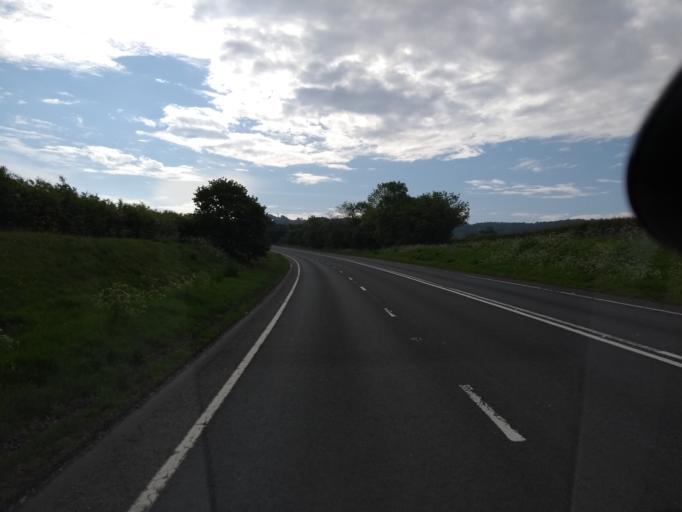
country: GB
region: England
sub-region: Devon
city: Axminster
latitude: 50.7684
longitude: -3.0006
